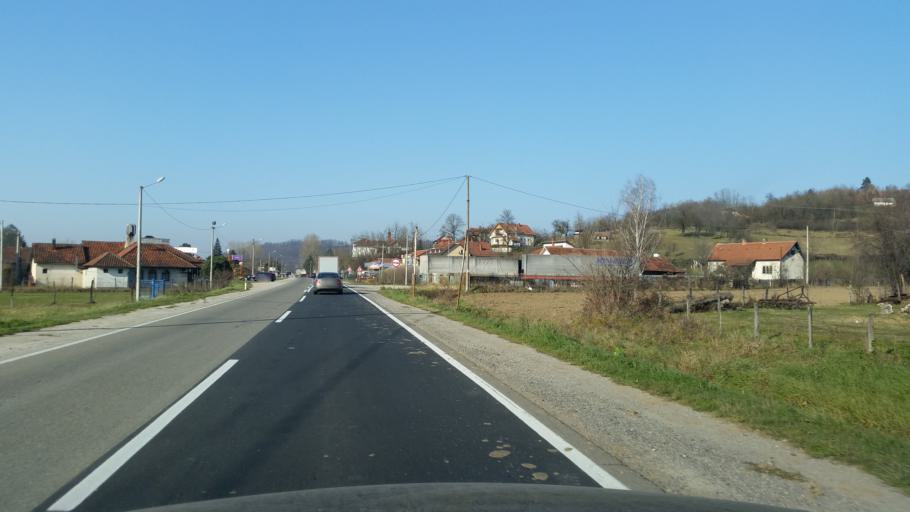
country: RS
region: Central Serbia
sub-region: Kolubarski Okrug
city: Lajkovac
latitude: 44.3348
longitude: 20.2147
